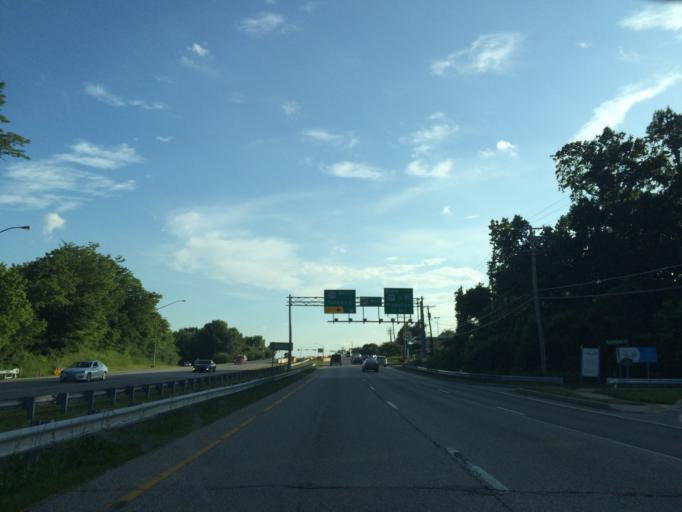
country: US
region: Maryland
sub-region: Howard County
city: Ellicott City
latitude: 39.2813
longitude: -76.8131
